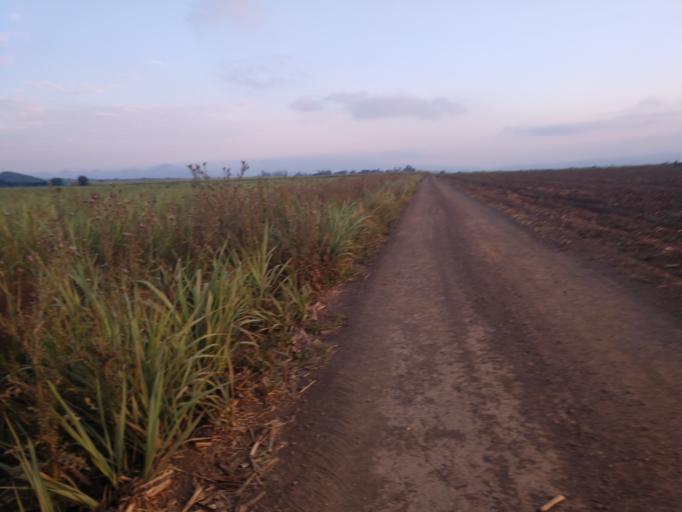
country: MX
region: Nayarit
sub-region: Tepic
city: La Corregidora
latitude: 21.4775
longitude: -104.8066
